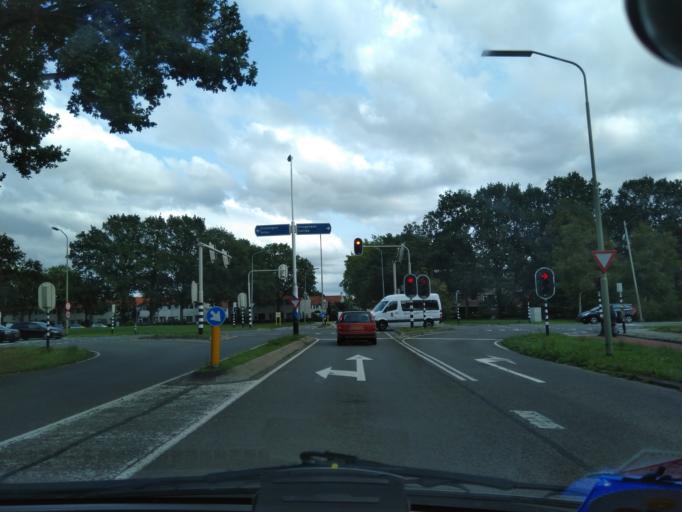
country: NL
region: Drenthe
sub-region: Gemeente Assen
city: Assen
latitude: 53.0082
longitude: 6.5481
